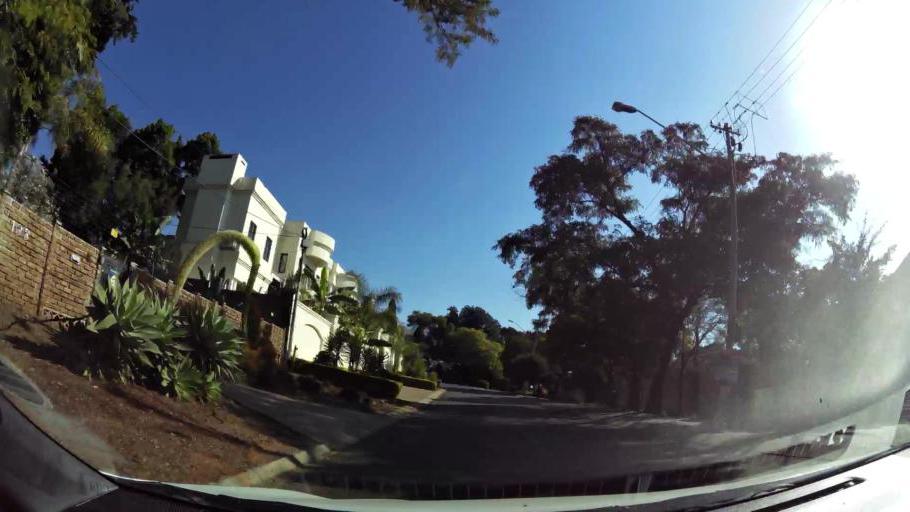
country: ZA
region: Gauteng
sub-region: City of Tshwane Metropolitan Municipality
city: Pretoria
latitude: -25.7874
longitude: 28.2584
